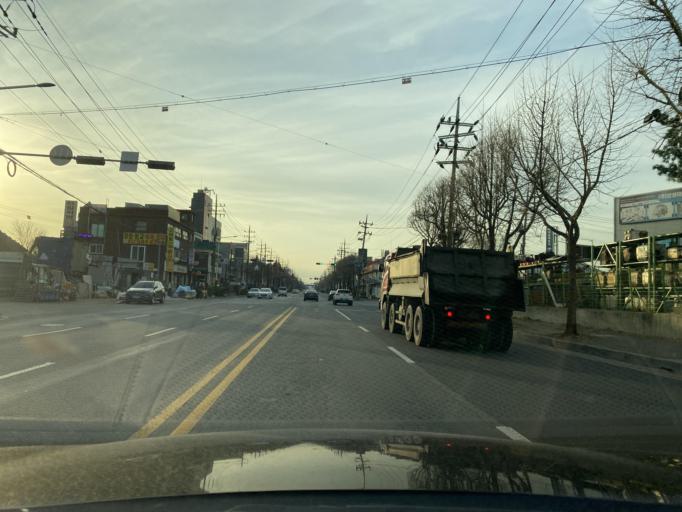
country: KR
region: Incheon
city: Incheon
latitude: 37.4992
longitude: 126.6598
